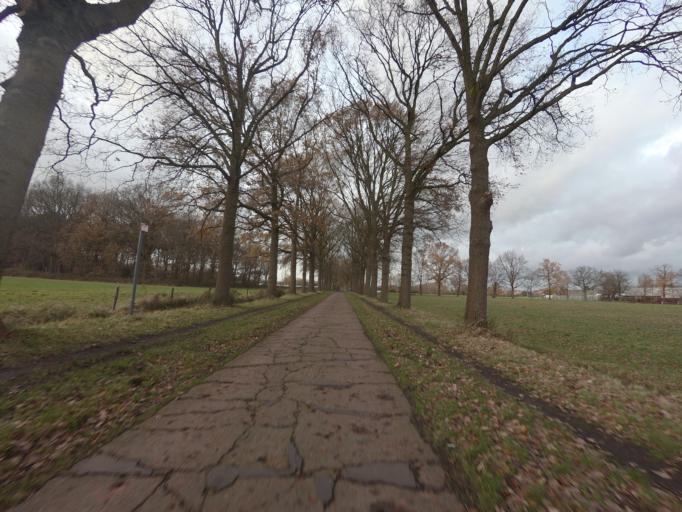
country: BE
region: Flanders
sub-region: Provincie Antwerpen
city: Hoboken
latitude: 51.1562
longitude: 4.3603
